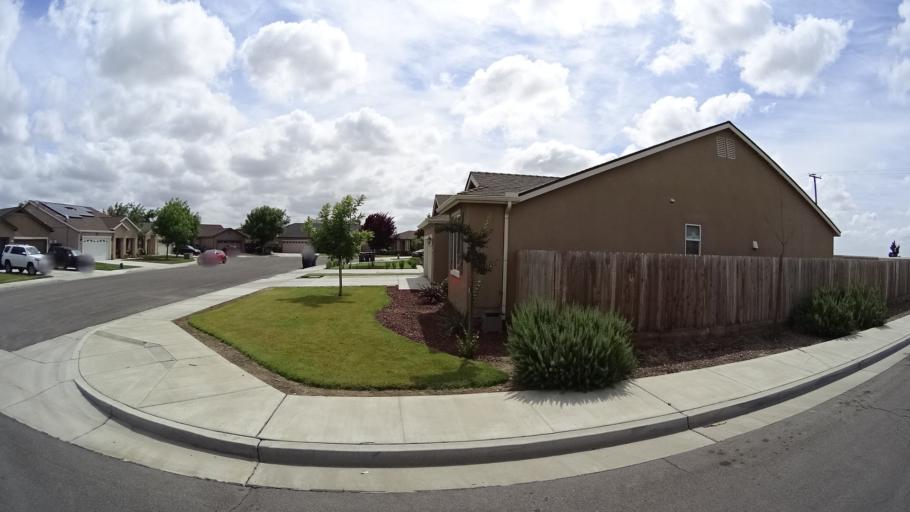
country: US
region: California
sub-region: Kings County
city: Hanford
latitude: 36.3060
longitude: -119.6676
